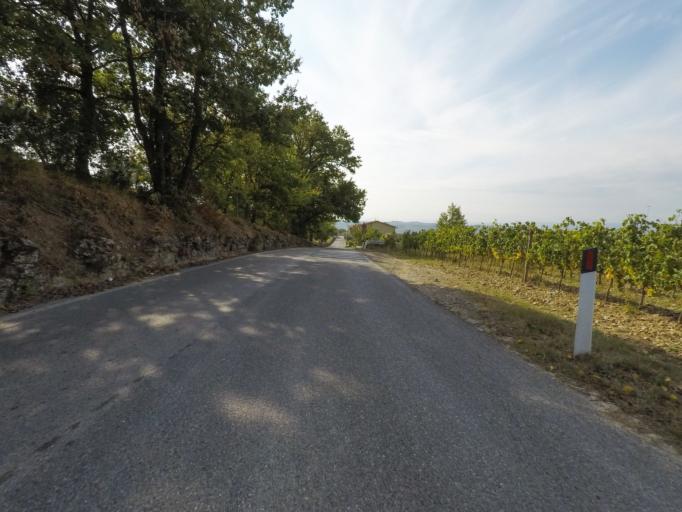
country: IT
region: Tuscany
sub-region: Provincia di Siena
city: Belverde
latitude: 43.3952
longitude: 11.3474
